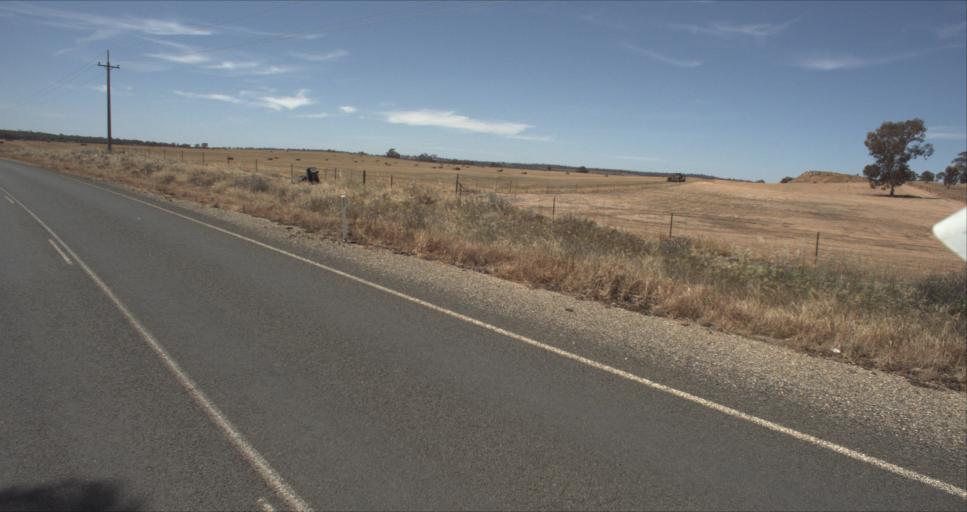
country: AU
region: New South Wales
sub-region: Leeton
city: Leeton
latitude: -34.6581
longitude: 146.4575
